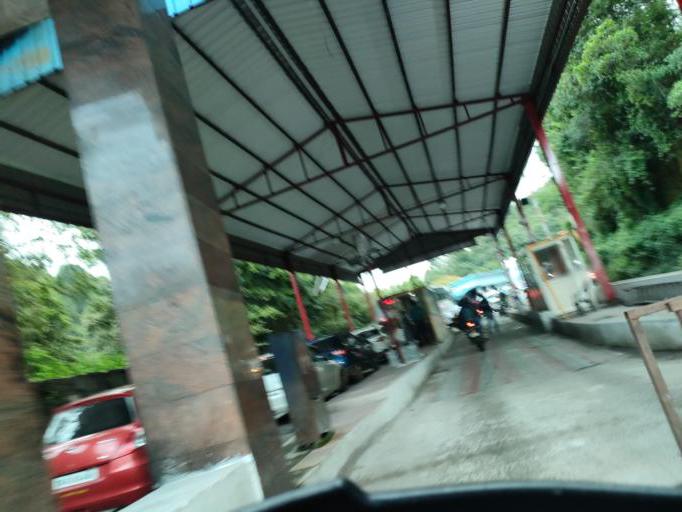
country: IN
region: Tamil Nadu
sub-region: Dindigul
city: Kodaikanal
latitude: 10.2418
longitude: 77.5121
